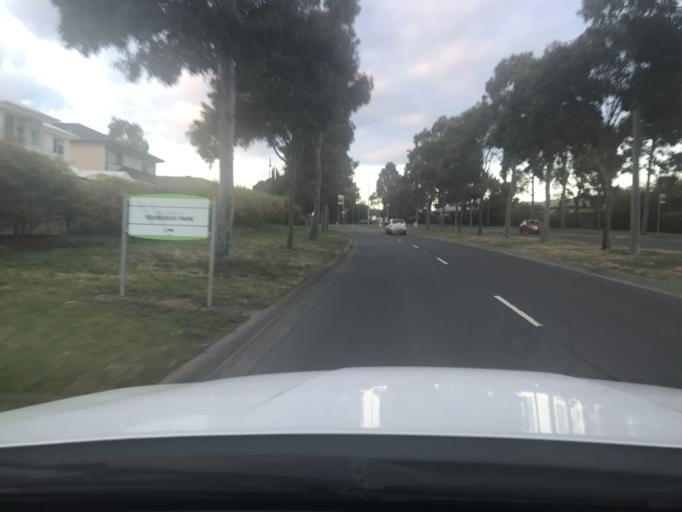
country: AU
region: Victoria
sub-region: Hume
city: Meadow Heights
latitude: -37.6394
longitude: 144.9239
